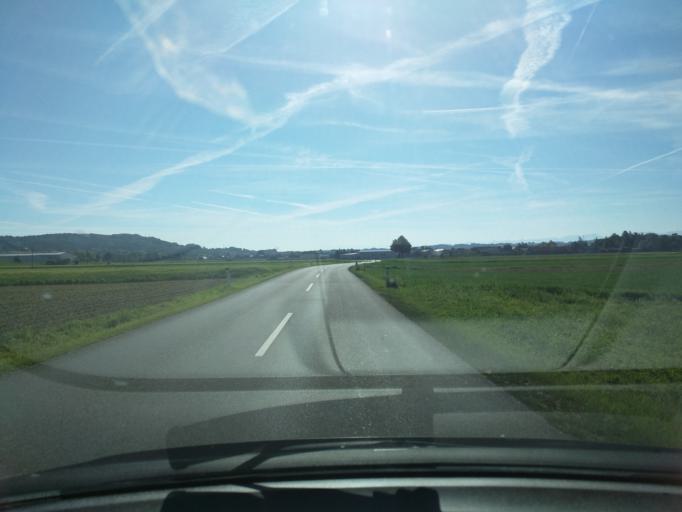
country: AT
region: Lower Austria
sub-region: Politischer Bezirk Melk
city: Blindenmarkt
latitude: 48.1304
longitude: 14.9702
